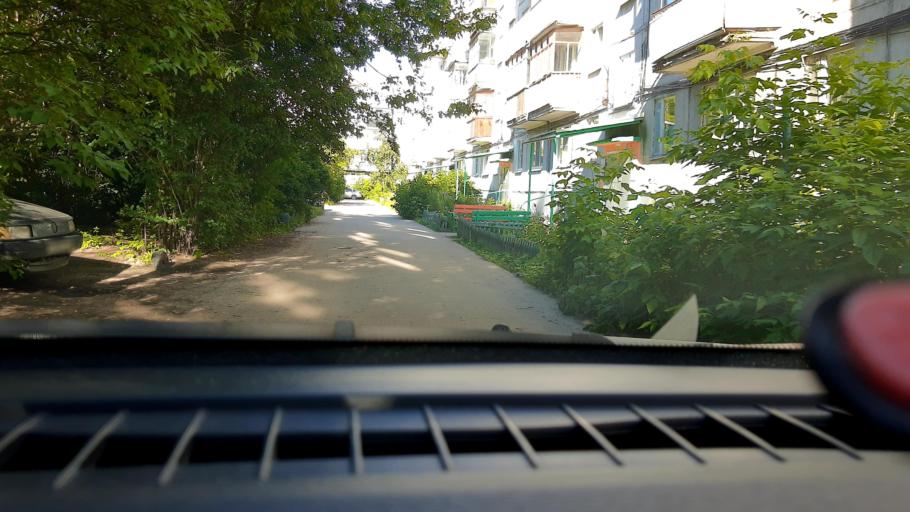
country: RU
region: Nizjnij Novgorod
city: Dzerzhinsk
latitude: 56.2269
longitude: 43.4235
